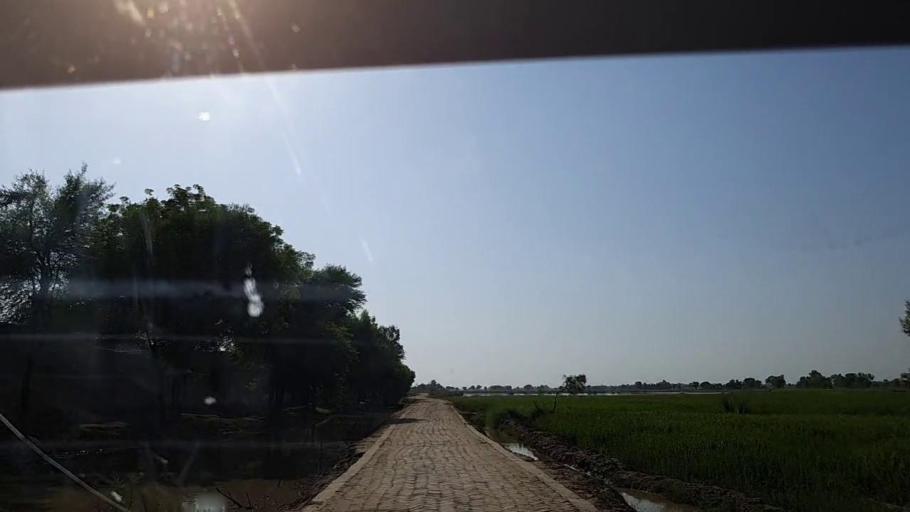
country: PK
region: Sindh
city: Tangwani
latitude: 28.2150
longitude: 68.9753
